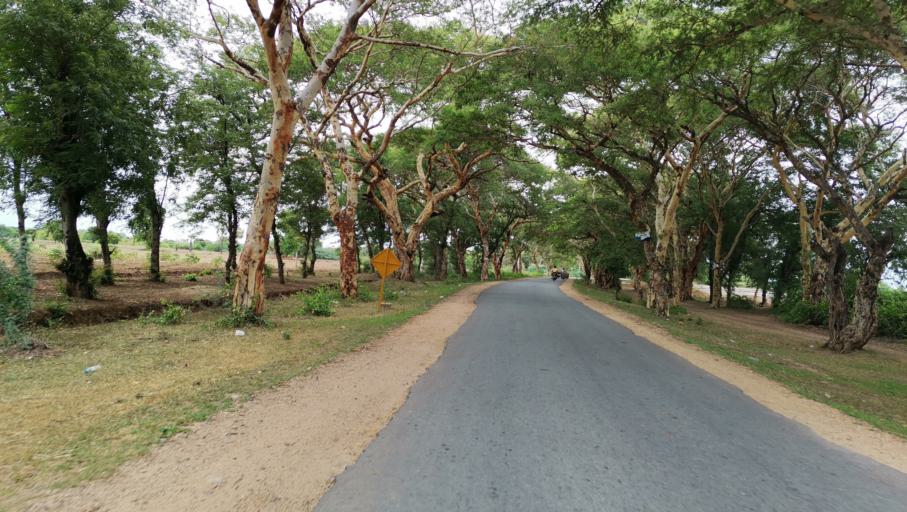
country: MM
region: Sagain
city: Monywa
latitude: 21.8514
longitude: 95.4334
